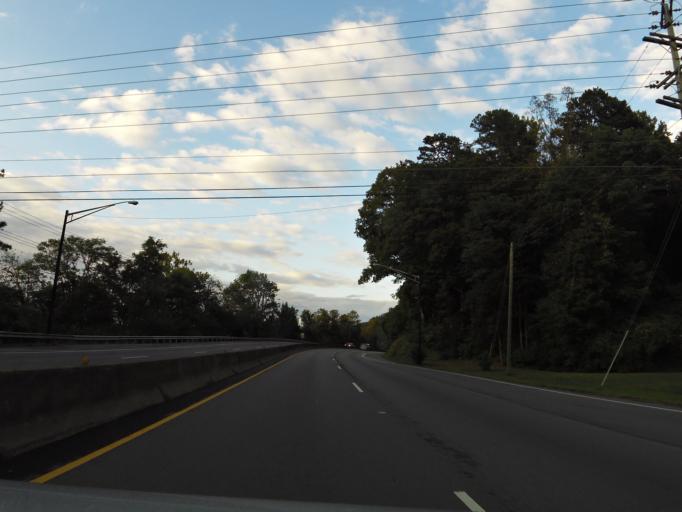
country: US
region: Tennessee
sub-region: Knox County
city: Knoxville
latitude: 35.9254
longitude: -83.9540
